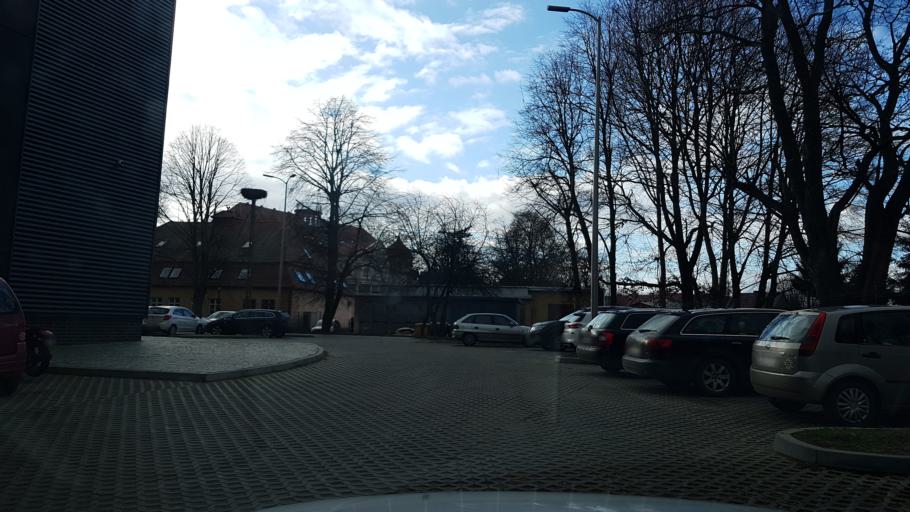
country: PL
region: West Pomeranian Voivodeship
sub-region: Powiat drawski
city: Drawsko Pomorskie
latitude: 53.5266
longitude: 15.8195
